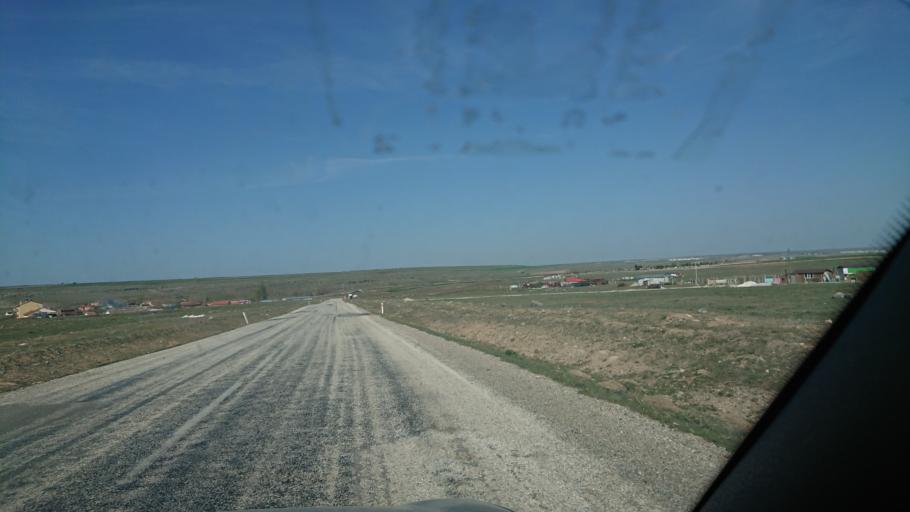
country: TR
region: Eskisehir
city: Eskisehir
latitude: 39.6732
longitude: 30.4795
